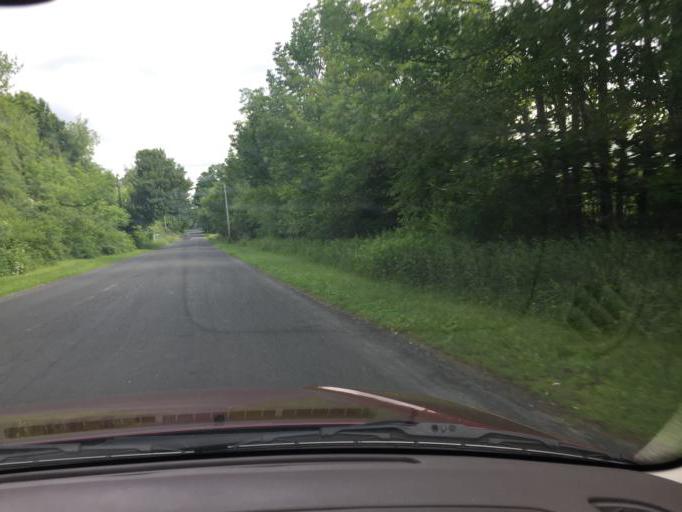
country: US
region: Connecticut
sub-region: Litchfield County
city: Litchfield
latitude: 41.7742
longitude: -73.2562
